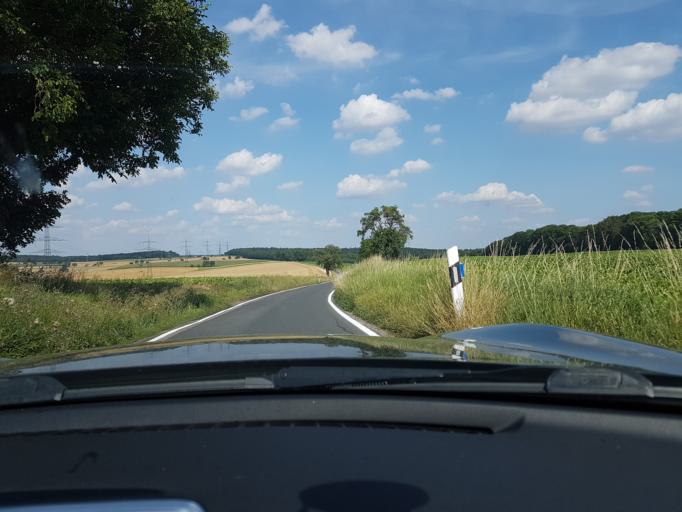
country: DE
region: Baden-Wuerttemberg
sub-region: Karlsruhe Region
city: Mosbach
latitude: 49.3323
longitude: 9.1689
